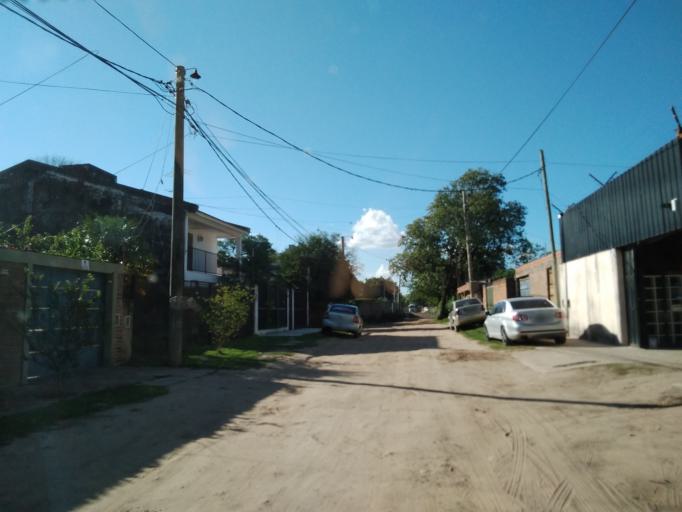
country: AR
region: Corrientes
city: Corrientes
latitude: -27.4796
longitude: -58.8522
